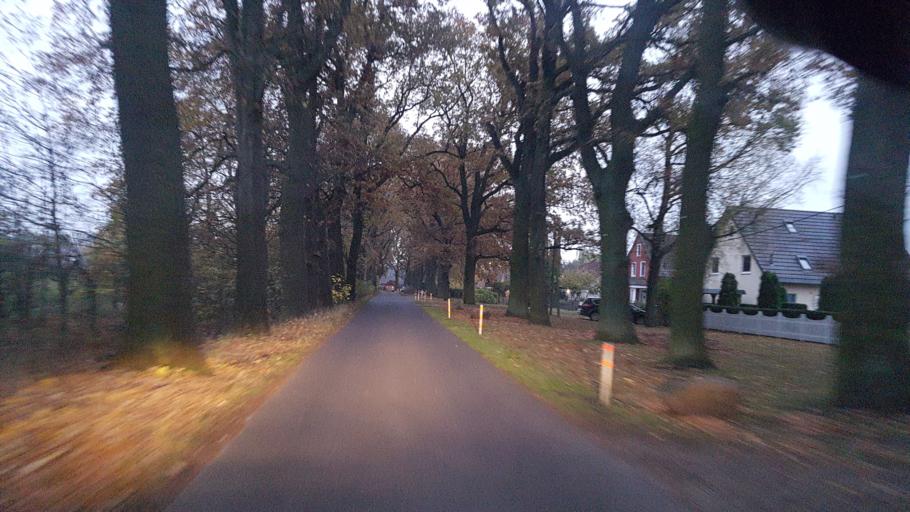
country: DE
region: Brandenburg
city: Nauen
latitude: 52.6391
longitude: 12.9011
